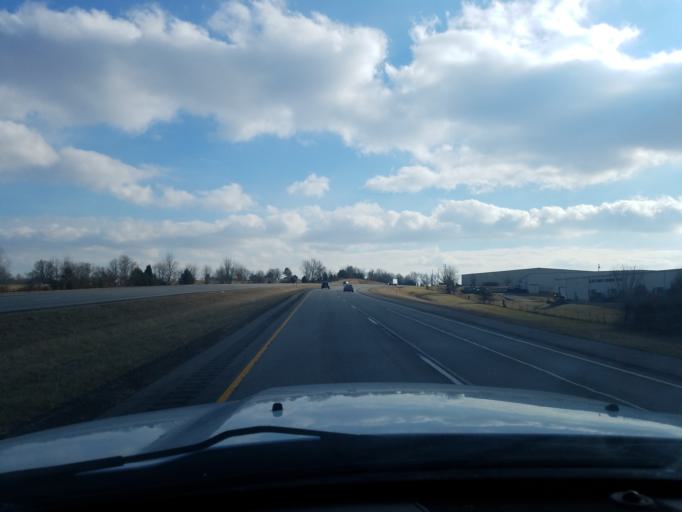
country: US
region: Kentucky
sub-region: Hardin County
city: Elizabethtown
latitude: 37.6605
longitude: -85.8373
